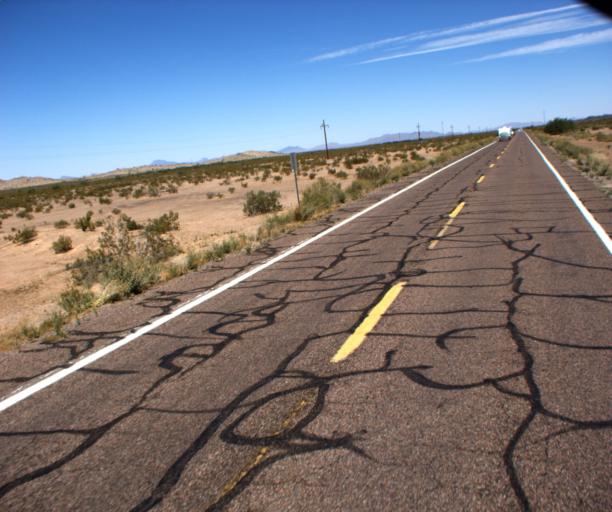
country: US
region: Arizona
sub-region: Maricopa County
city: Gila Bend
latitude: 32.7661
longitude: -112.8184
